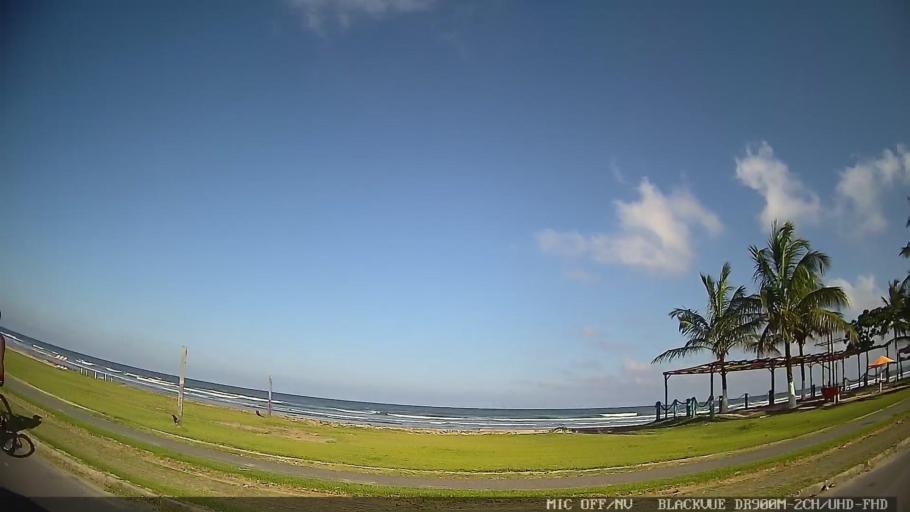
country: BR
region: Sao Paulo
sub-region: Peruibe
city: Peruibe
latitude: -24.2932
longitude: -46.9595
